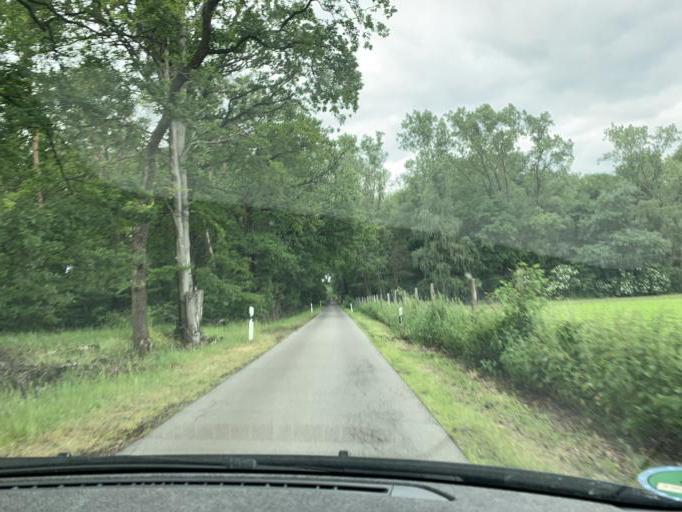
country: DE
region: North Rhine-Westphalia
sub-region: Regierungsbezirk Koln
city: Merzenich
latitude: 50.8740
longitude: 6.5142
